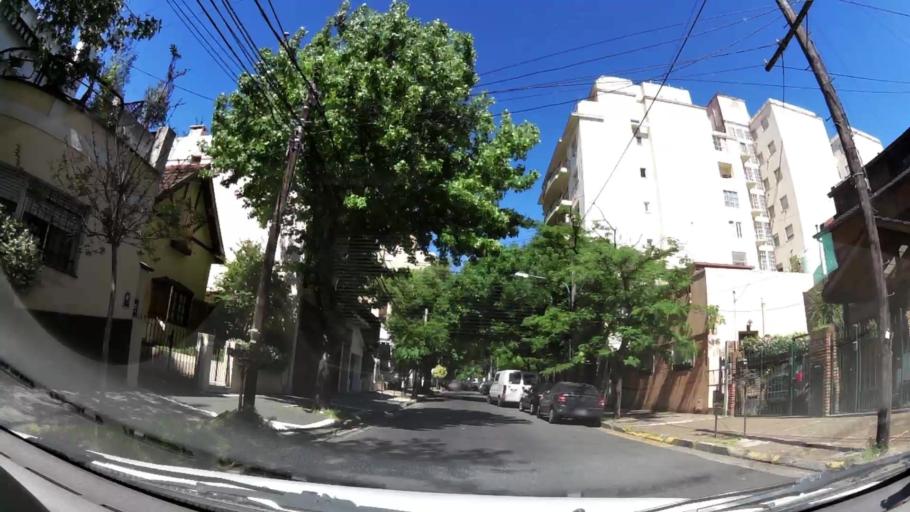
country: AR
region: Buenos Aires
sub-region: Partido de Vicente Lopez
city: Olivos
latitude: -34.5165
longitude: -58.4892
